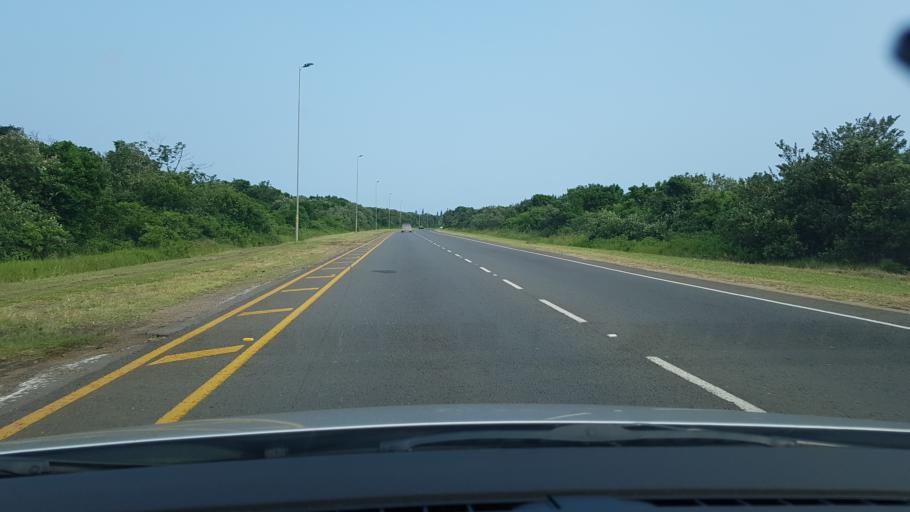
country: ZA
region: KwaZulu-Natal
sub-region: uThungulu District Municipality
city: Richards Bay
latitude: -28.7764
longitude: 32.0767
